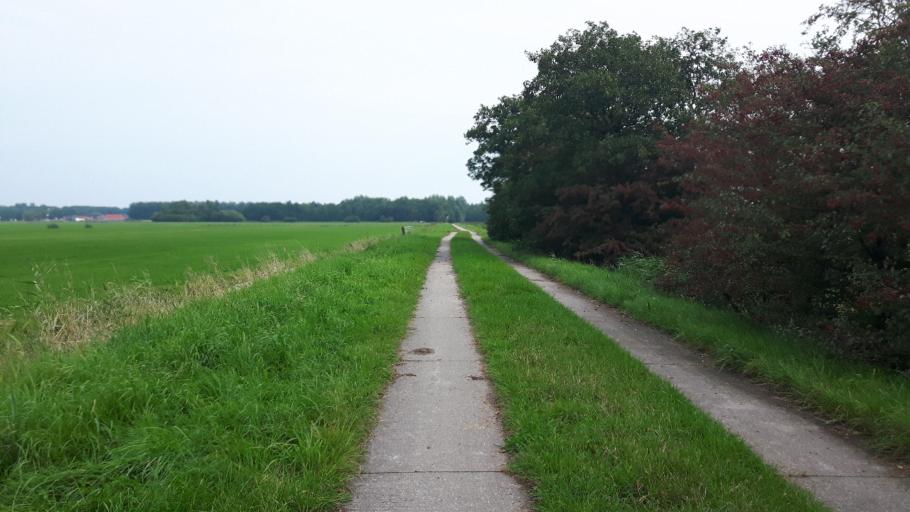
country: NL
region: Groningen
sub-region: Gemeente Bedum
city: Bedum
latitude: 53.3310
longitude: 6.5714
